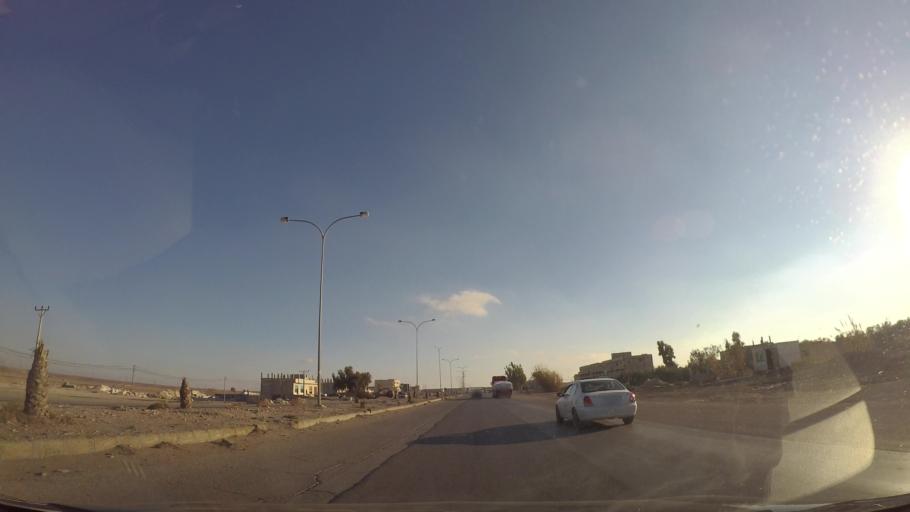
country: JO
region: Tafielah
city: Busayra
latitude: 30.5876
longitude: 35.8018
